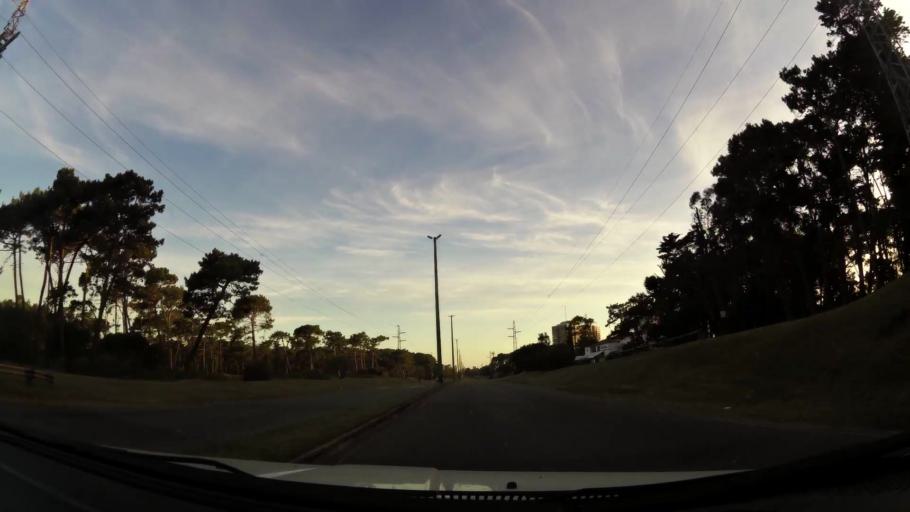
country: UY
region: Maldonado
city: Maldonado
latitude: -34.9269
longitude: -54.9409
